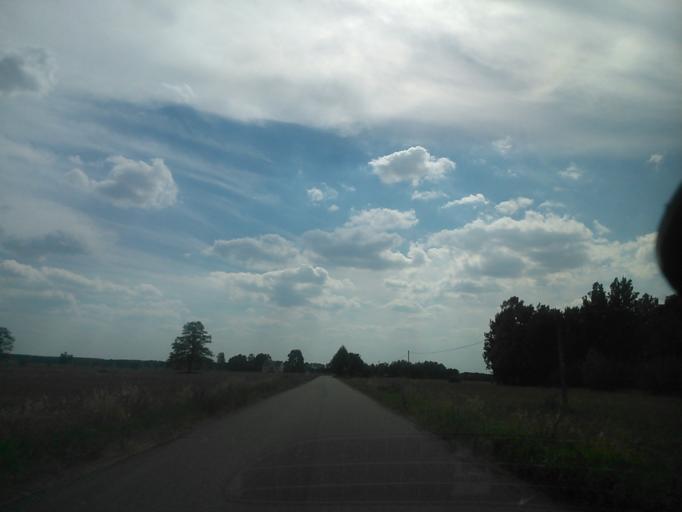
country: PL
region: Masovian Voivodeship
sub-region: Powiat ostrolecki
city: Czarnia
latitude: 53.3741
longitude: 21.1997
